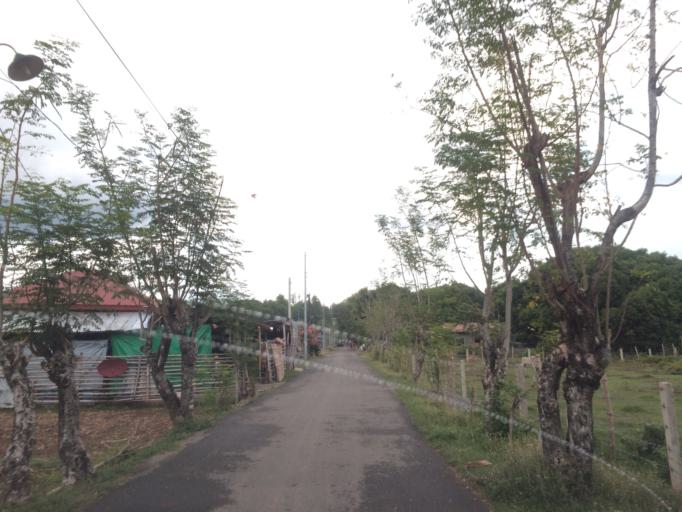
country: PH
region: Ilocos
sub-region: Province of Pangasinan
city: Anambongan
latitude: 15.8698
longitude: 120.3882
